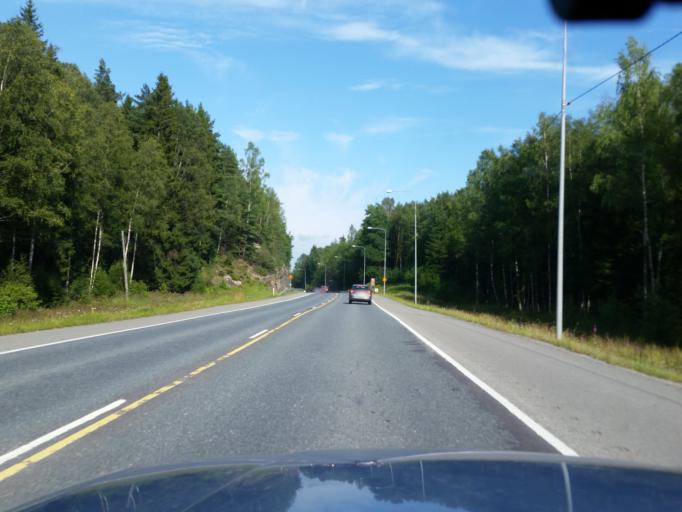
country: FI
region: Uusimaa
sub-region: Helsinki
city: Siuntio
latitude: 60.0965
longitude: 24.2800
